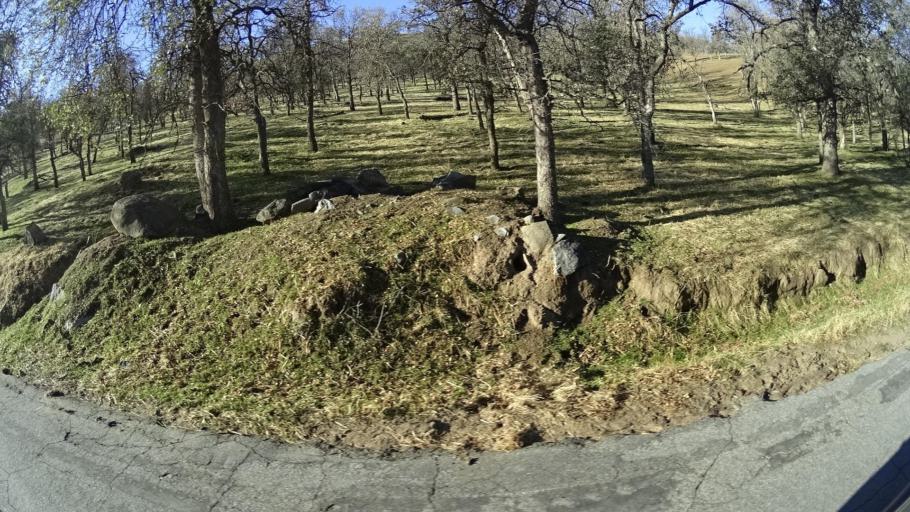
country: US
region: California
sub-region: Kern County
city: Alta Sierra
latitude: 35.7646
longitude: -118.8212
